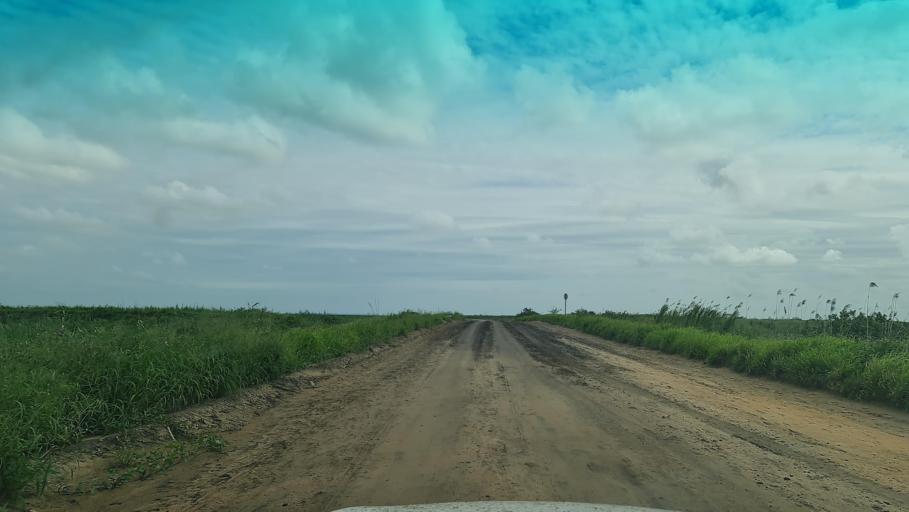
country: MZ
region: Maputo
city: Manhica
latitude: -25.4560
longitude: 32.8190
